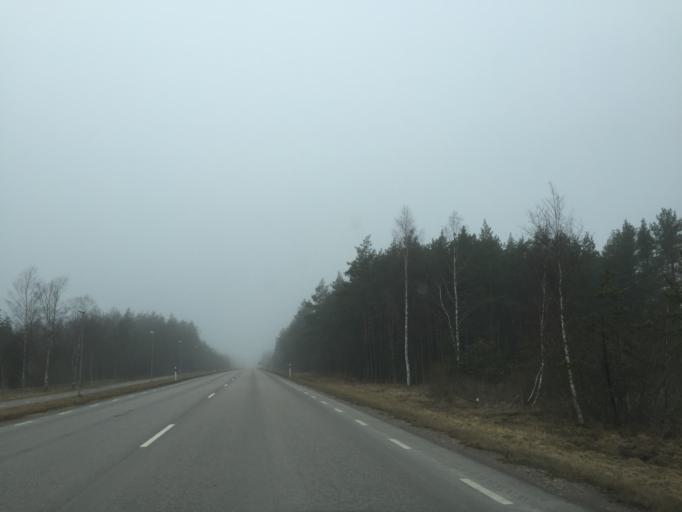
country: EE
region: Saare
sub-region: Kuressaare linn
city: Kuressaare
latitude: 58.2352
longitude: 22.4264
